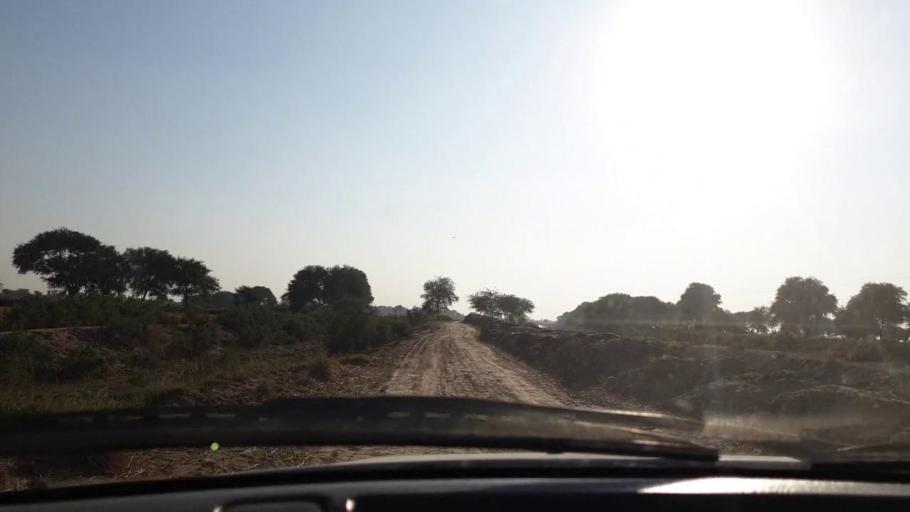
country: PK
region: Sindh
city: Bulri
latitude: 24.8086
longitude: 68.3972
